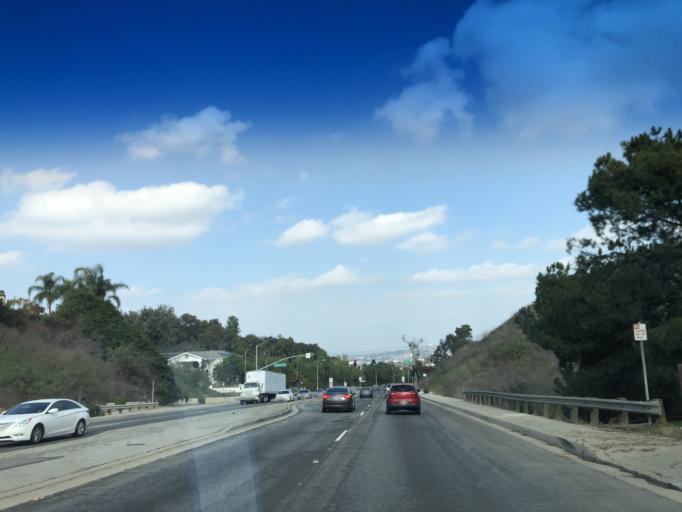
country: US
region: California
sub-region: Los Angeles County
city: Hacienda Heights
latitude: 33.9770
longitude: -117.9827
